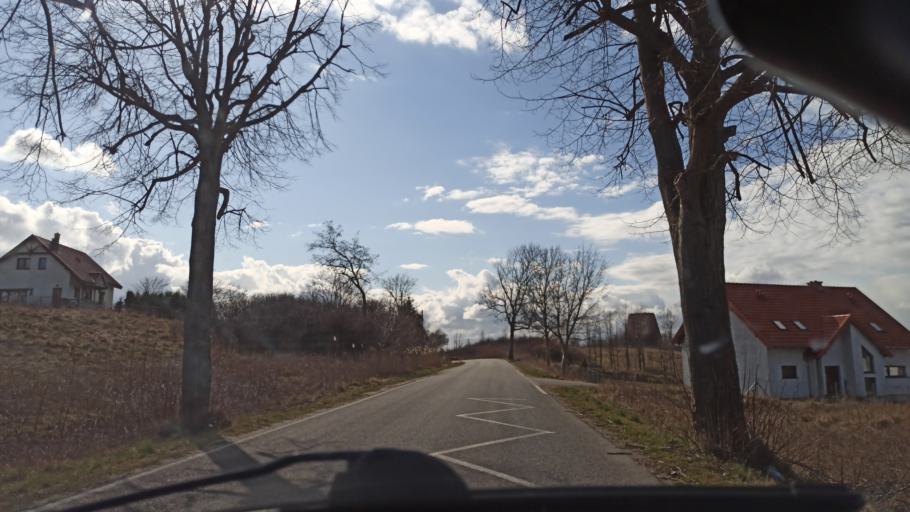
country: PL
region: Warmian-Masurian Voivodeship
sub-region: Powiat elblaski
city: Tolkmicko
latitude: 54.2709
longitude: 19.4780
